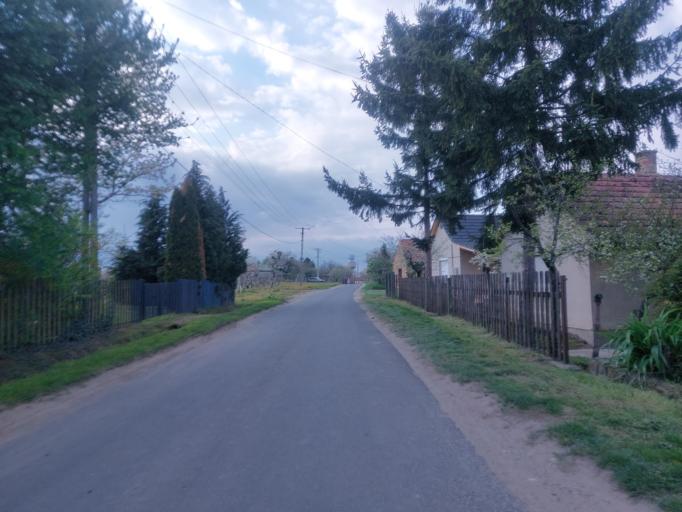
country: HU
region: Veszprem
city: Devecser
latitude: 47.1571
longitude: 17.3770
